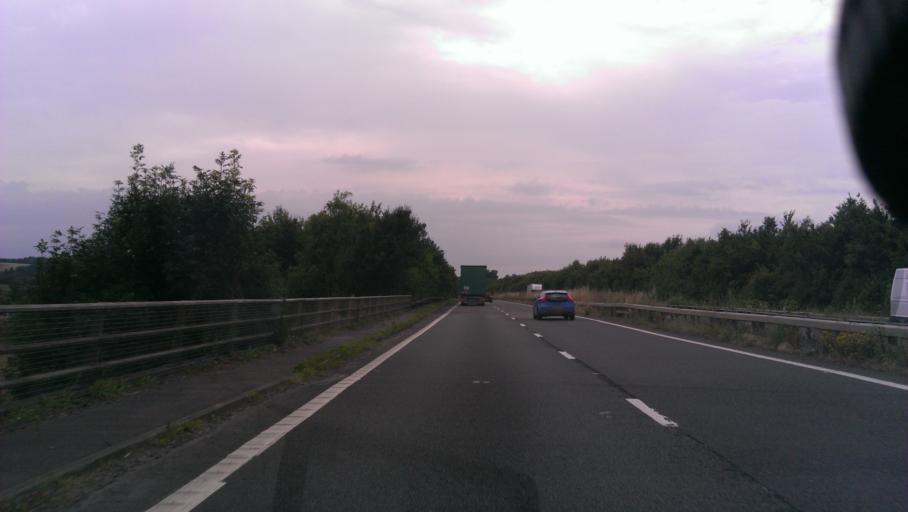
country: GB
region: England
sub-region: Kent
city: Canterbury
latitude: 51.2718
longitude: 1.0579
